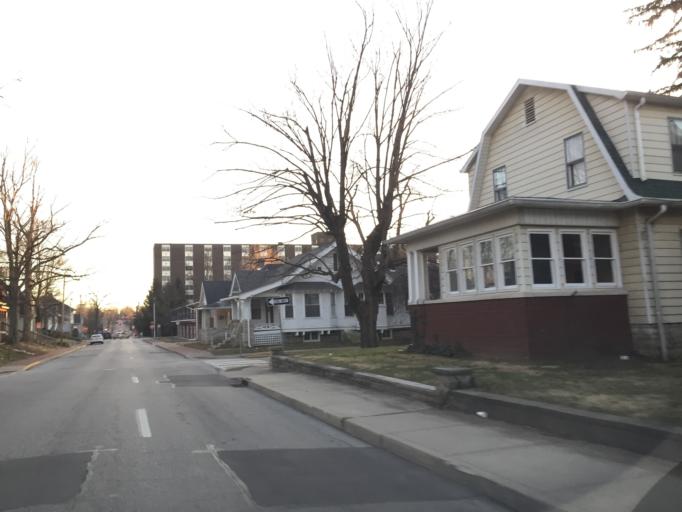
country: US
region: Indiana
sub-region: Monroe County
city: Bloomington
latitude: 39.1698
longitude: -86.5283
